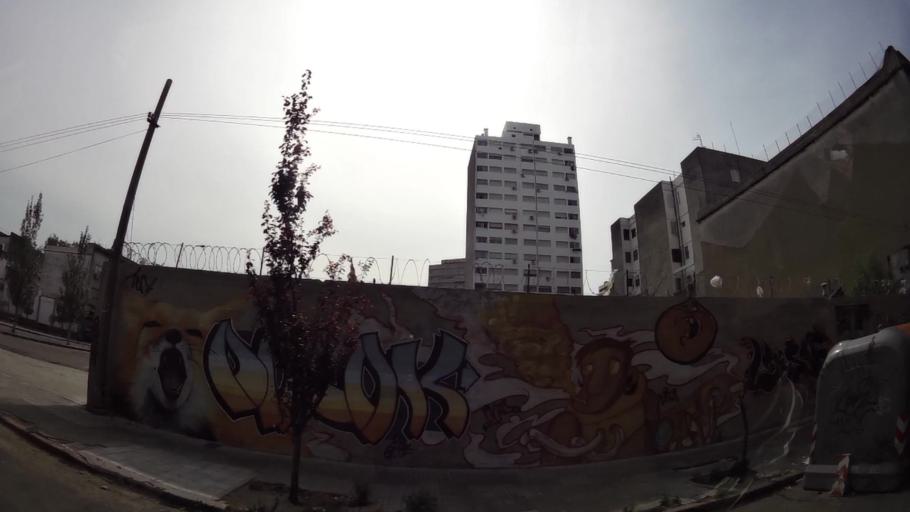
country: UY
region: Montevideo
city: Montevideo
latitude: -34.8997
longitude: -56.1932
